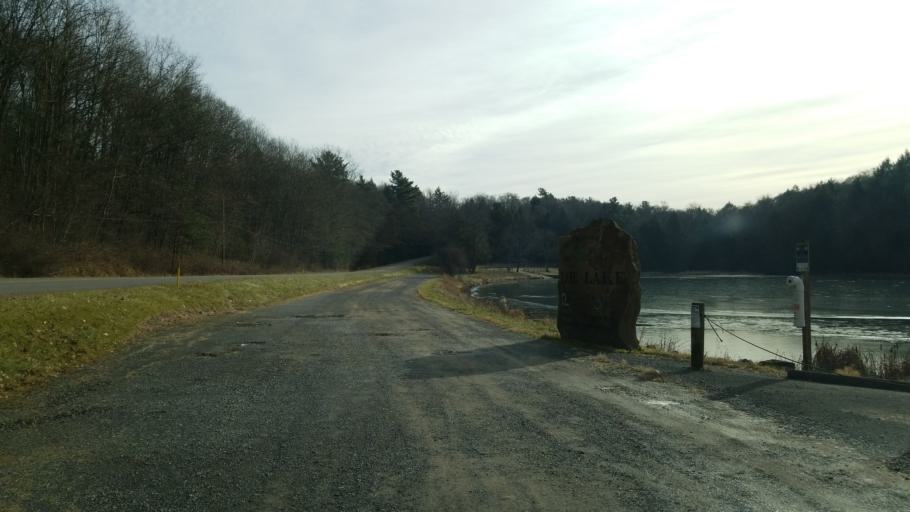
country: US
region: Pennsylvania
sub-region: Jefferson County
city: Albion
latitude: 40.9511
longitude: -78.9079
